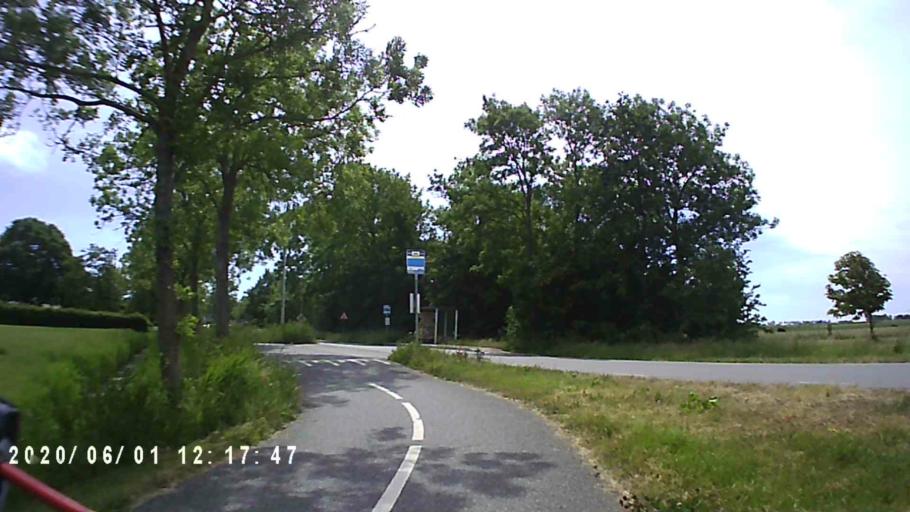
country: NL
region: Friesland
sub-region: Gemeente Harlingen
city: Harlingen
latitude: 53.1334
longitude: 5.4704
